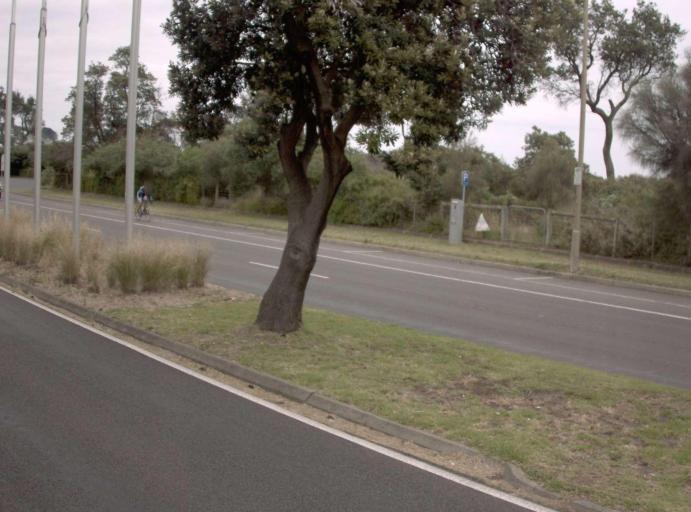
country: AU
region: Victoria
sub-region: Frankston
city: Frankston
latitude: -38.1493
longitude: 145.1155
